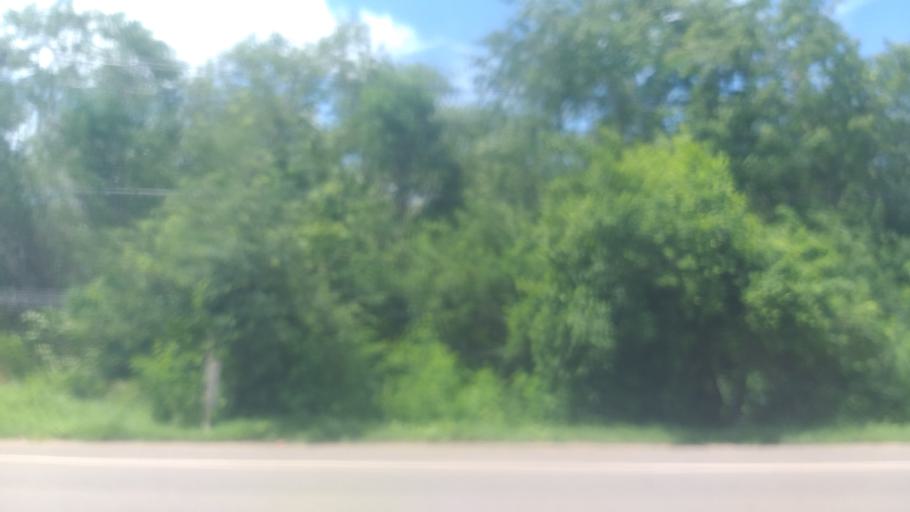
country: TH
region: Nakhon Ratchasima
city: Phra Thong Kham
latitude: 15.2950
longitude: 101.9873
